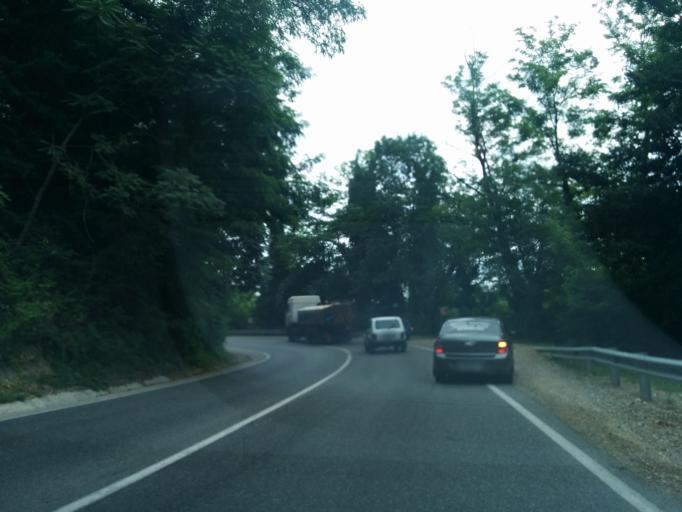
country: RU
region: Krasnodarskiy
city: Agoy
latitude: 44.1180
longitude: 39.0489
